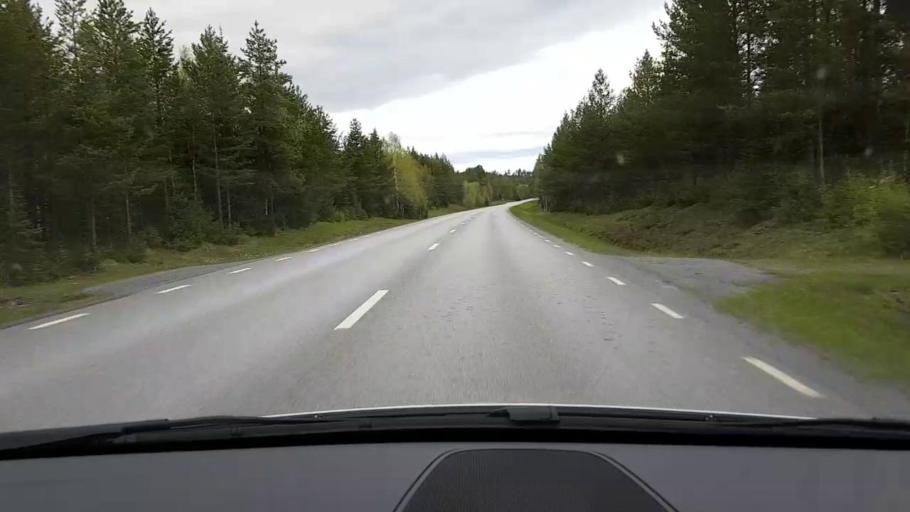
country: SE
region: Jaemtland
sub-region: Krokoms Kommun
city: Valla
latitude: 63.2887
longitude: 13.9277
